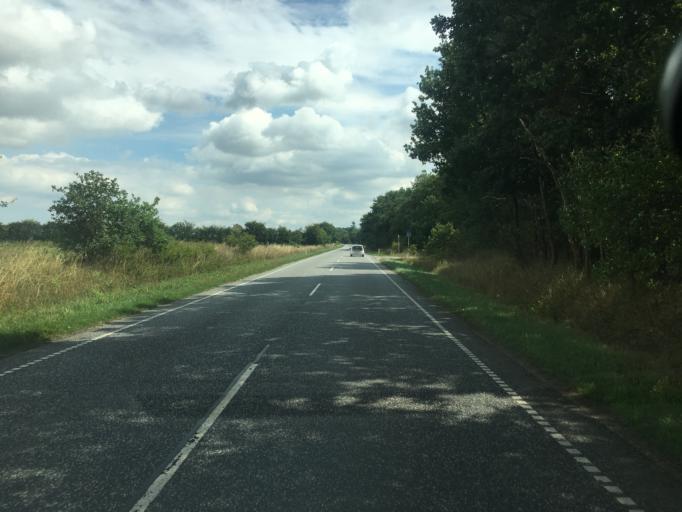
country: DK
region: South Denmark
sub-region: Aabenraa Kommune
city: Aabenraa
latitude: 54.9817
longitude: 9.3582
